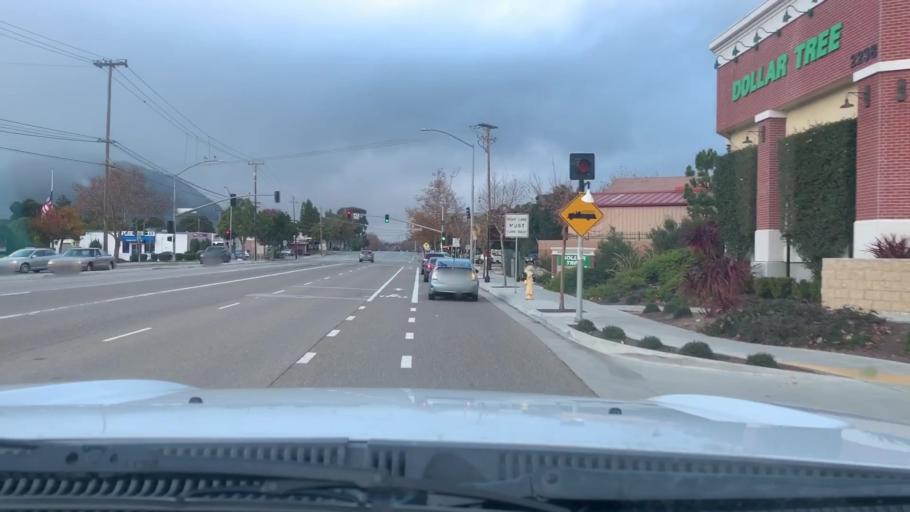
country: US
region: California
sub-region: San Luis Obispo County
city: San Luis Obispo
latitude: 35.2692
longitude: -120.6559
